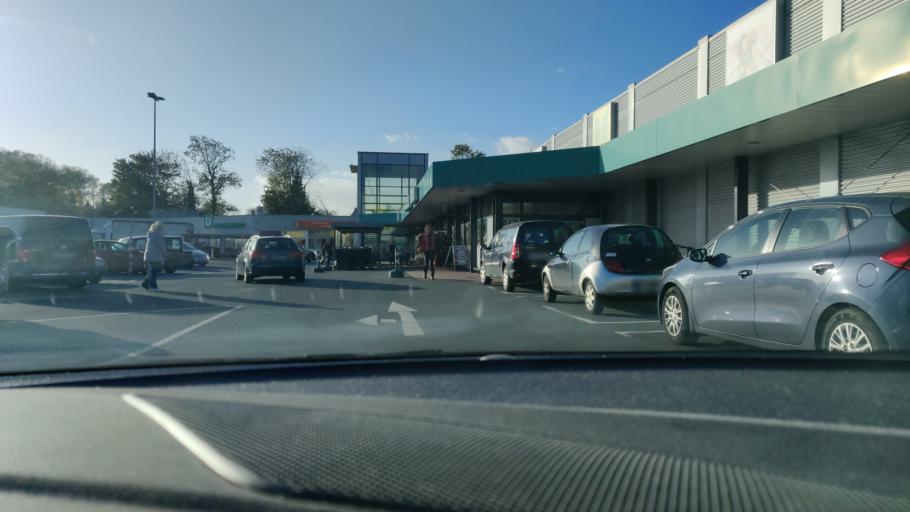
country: DE
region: Lower Saxony
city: Cuxhaven
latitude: 53.8451
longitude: 8.6923
